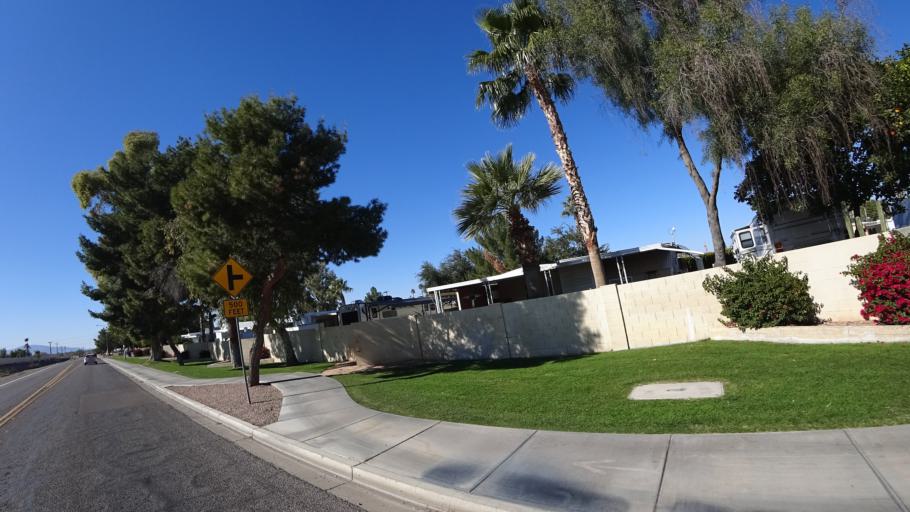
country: US
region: Arizona
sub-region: Maricopa County
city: Surprise
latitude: 33.6526
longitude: -112.2934
